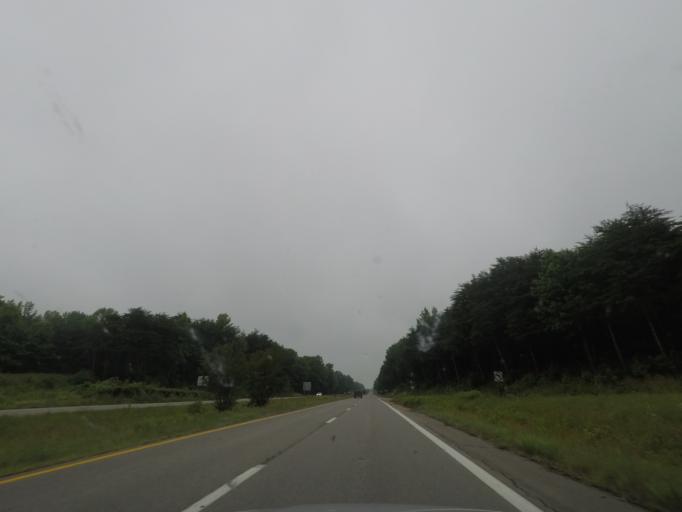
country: US
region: Virginia
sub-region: Charlotte County
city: Charlotte Court House
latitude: 37.0374
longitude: -78.4702
